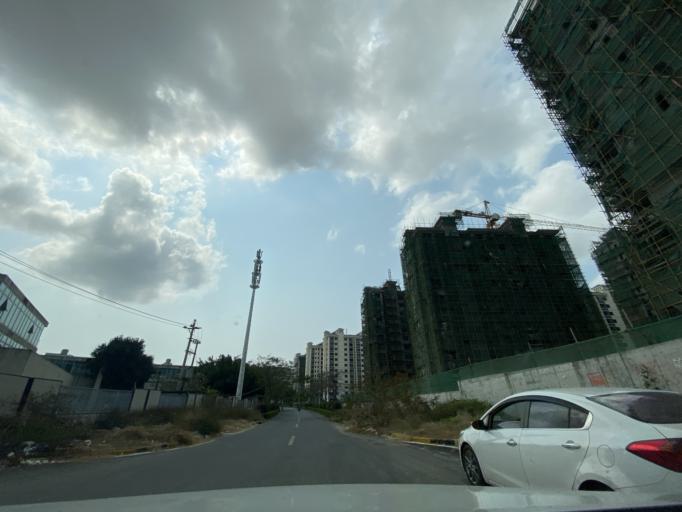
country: CN
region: Hainan
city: Yingzhou
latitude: 18.4130
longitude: 109.8514
